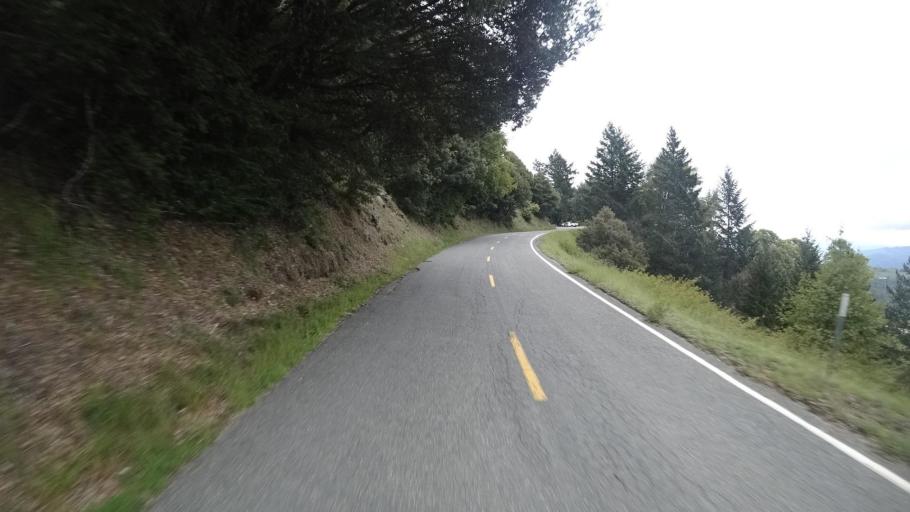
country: US
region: California
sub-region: Humboldt County
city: Redway
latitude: 40.1123
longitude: -123.7334
